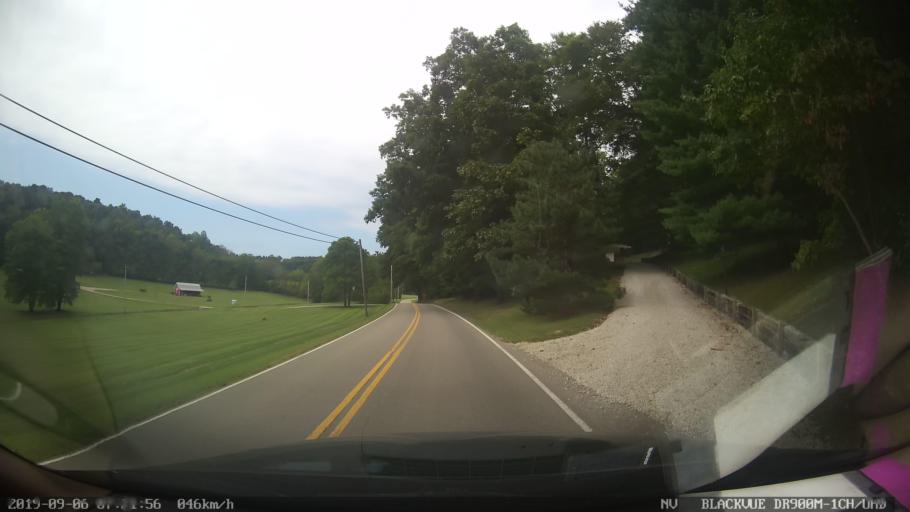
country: US
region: Ohio
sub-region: Licking County
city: Newark
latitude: 40.1366
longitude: -82.3764
